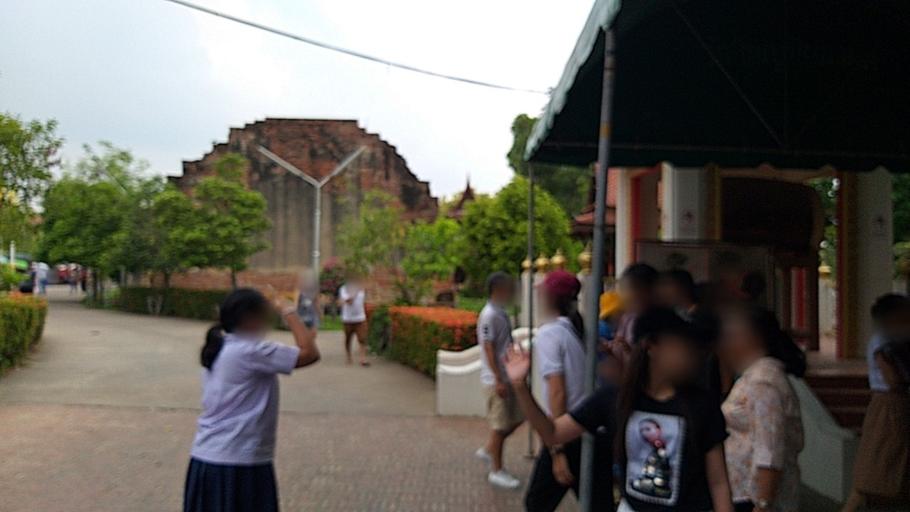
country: TH
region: Phra Nakhon Si Ayutthaya
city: Phra Nakhon Si Ayutthaya
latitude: 14.3457
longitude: 100.5932
